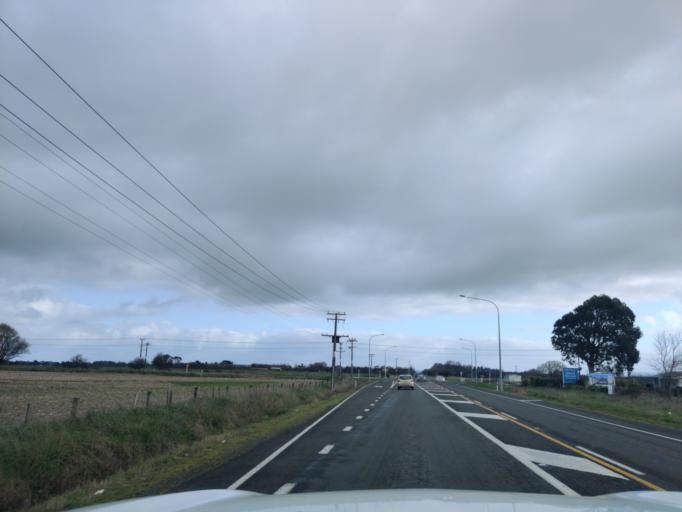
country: NZ
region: Manawatu-Wanganui
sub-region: Palmerston North City
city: Palmerston North
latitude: -40.3337
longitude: 175.5916
